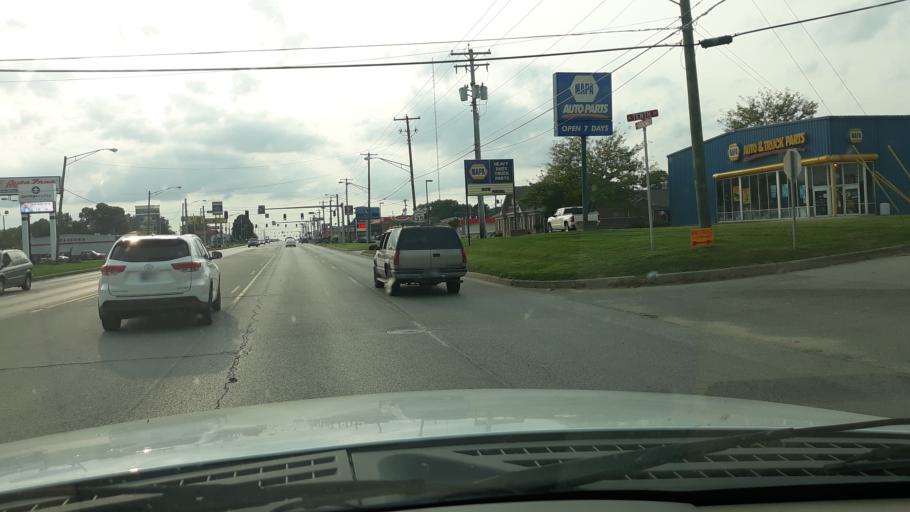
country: US
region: Indiana
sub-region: Gibson County
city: Princeton
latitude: 38.3555
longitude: -87.5841
